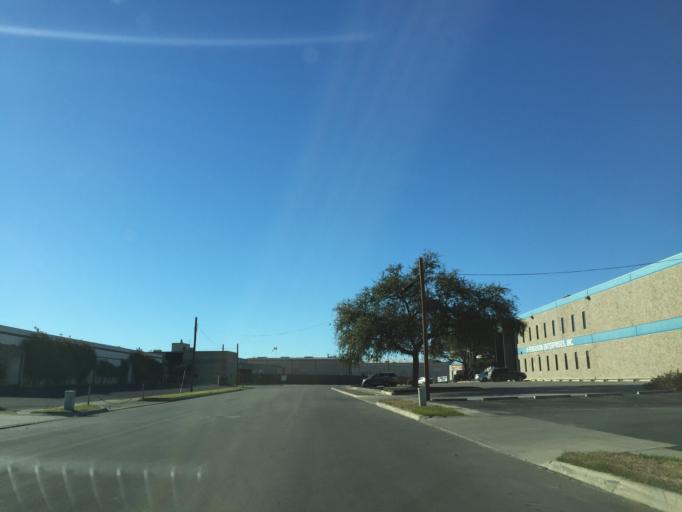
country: US
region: Texas
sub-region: Bexar County
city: Castle Hills
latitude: 29.5526
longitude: -98.4905
